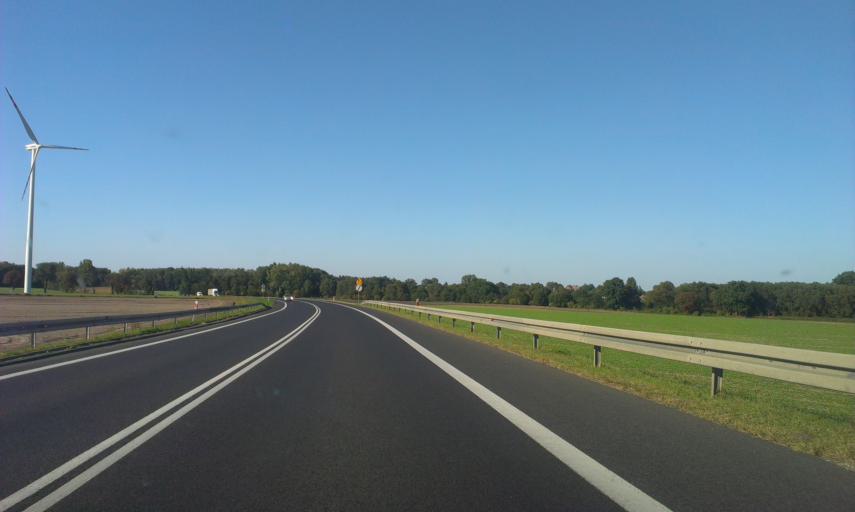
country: PL
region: Kujawsko-Pomorskie
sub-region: Powiat torunski
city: Chelmza
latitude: 53.2012
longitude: 18.5659
